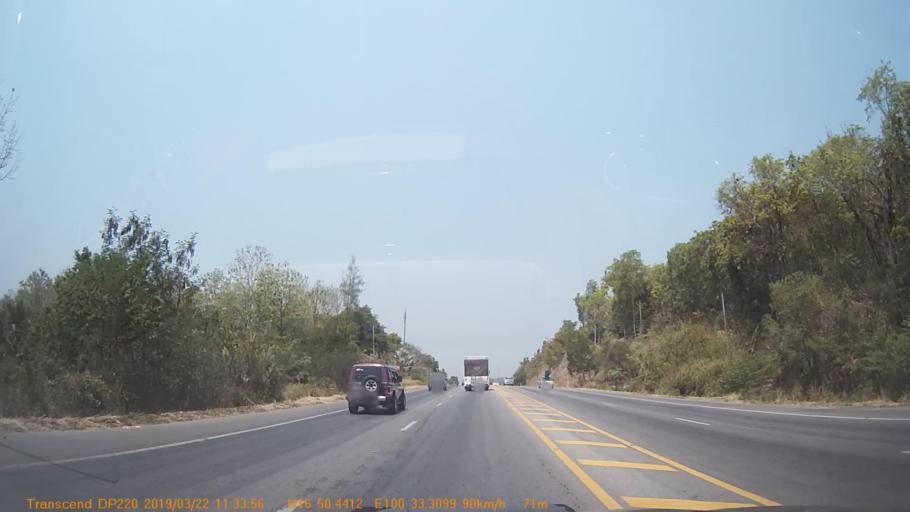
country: TH
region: Phitsanulok
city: Wang Thong
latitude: 16.8408
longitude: 100.5549
